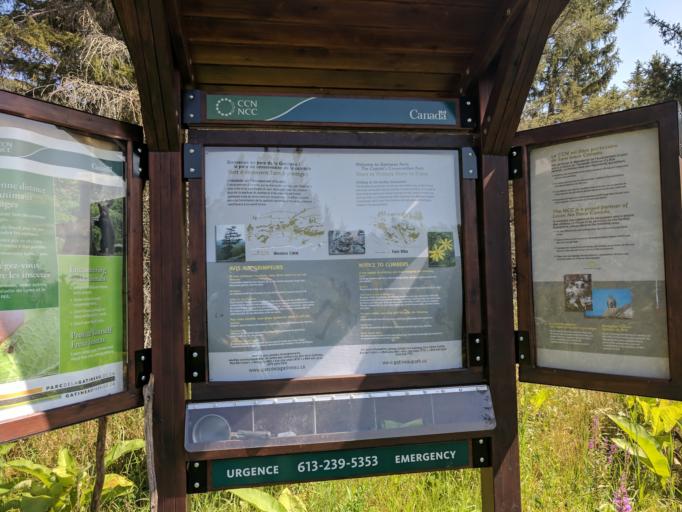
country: CA
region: Quebec
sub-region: Outaouais
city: Wakefield
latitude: 45.5304
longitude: -75.9861
